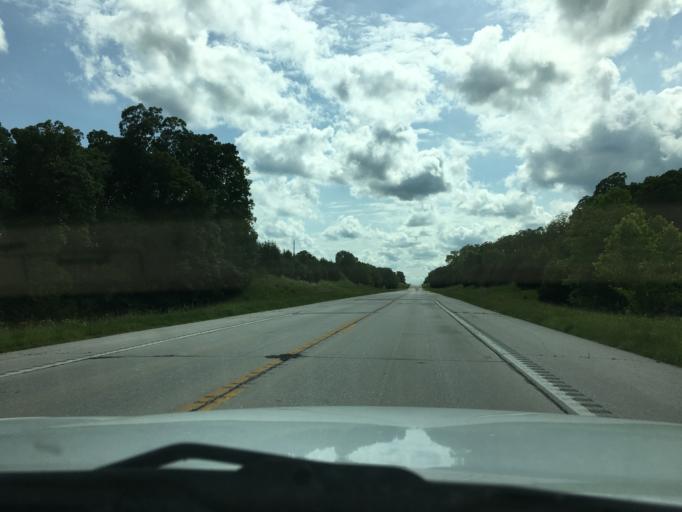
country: US
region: Missouri
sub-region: Franklin County
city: Gerald
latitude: 38.4219
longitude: -91.2831
